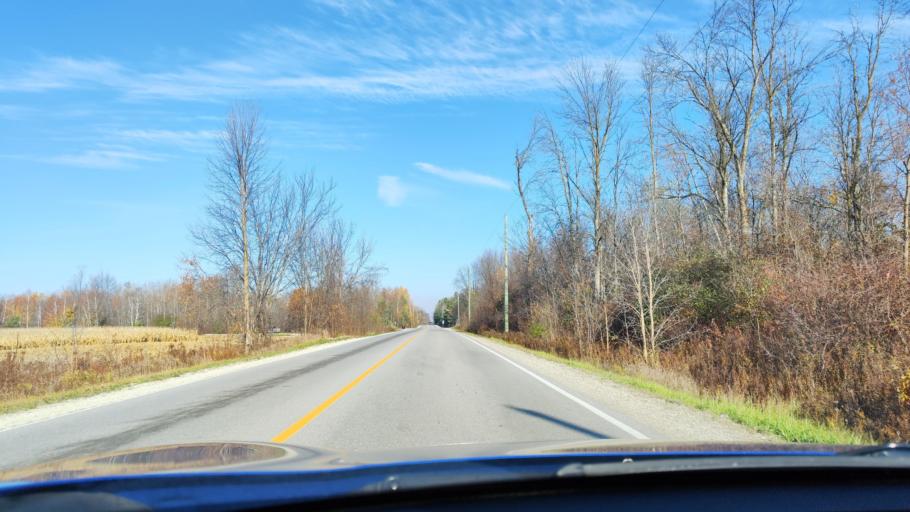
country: CA
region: Ontario
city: Wasaga Beach
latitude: 44.4034
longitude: -80.0585
